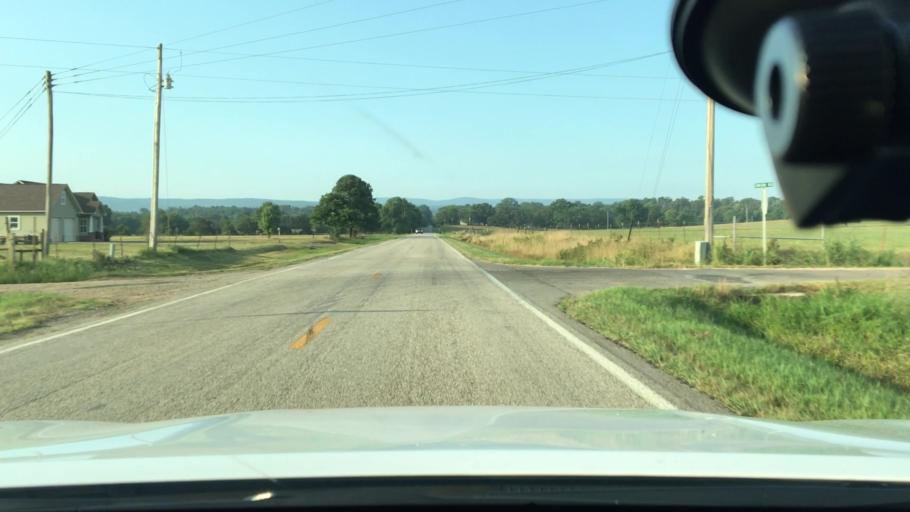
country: US
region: Arkansas
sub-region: Logan County
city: Paris
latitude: 35.3233
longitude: -93.6322
